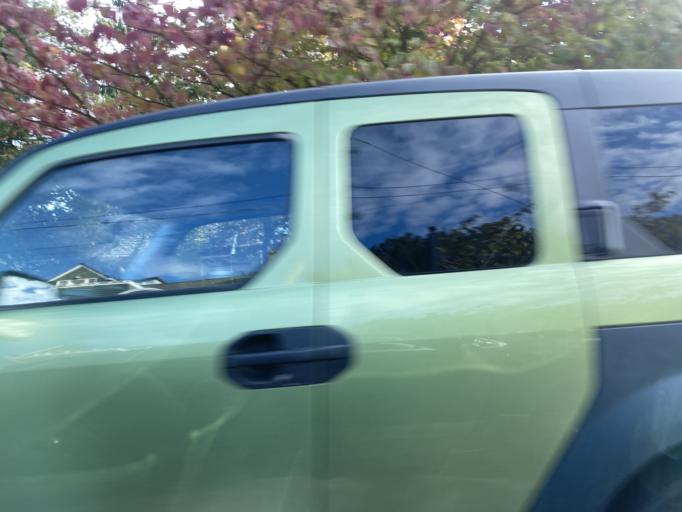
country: US
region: Washington
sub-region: King County
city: Seattle
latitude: 47.6492
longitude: -122.4036
